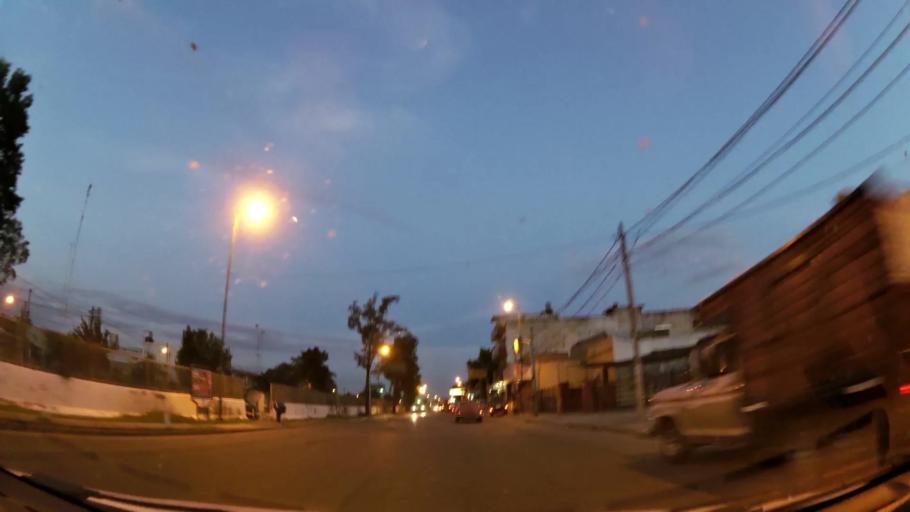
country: AR
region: Buenos Aires
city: Ituzaingo
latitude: -34.6617
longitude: -58.6723
